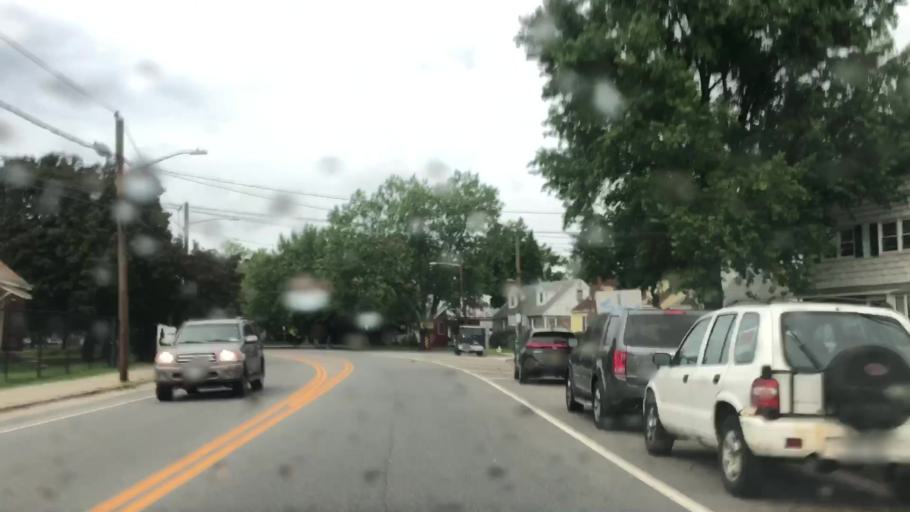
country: US
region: New York
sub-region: Nassau County
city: Stewart Manor
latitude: 40.7148
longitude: -73.6885
